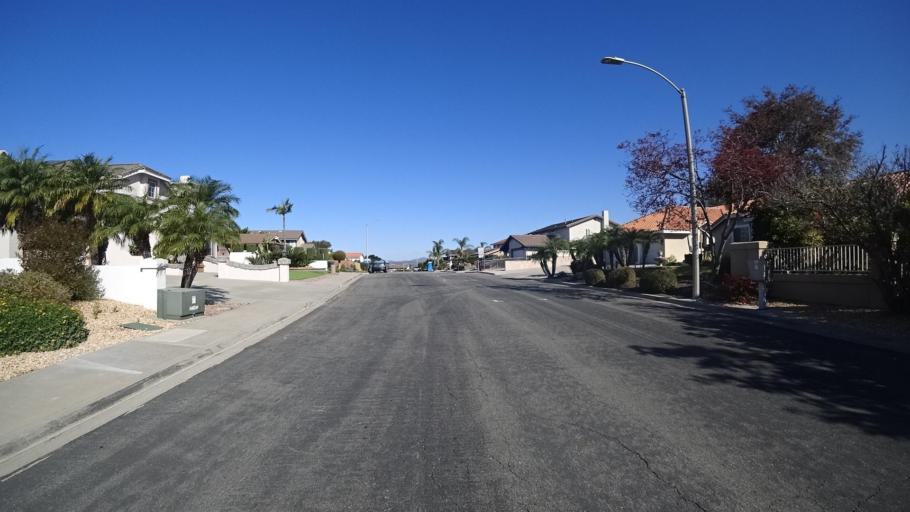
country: US
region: California
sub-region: San Diego County
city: Bonita
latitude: 32.6604
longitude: -116.9967
